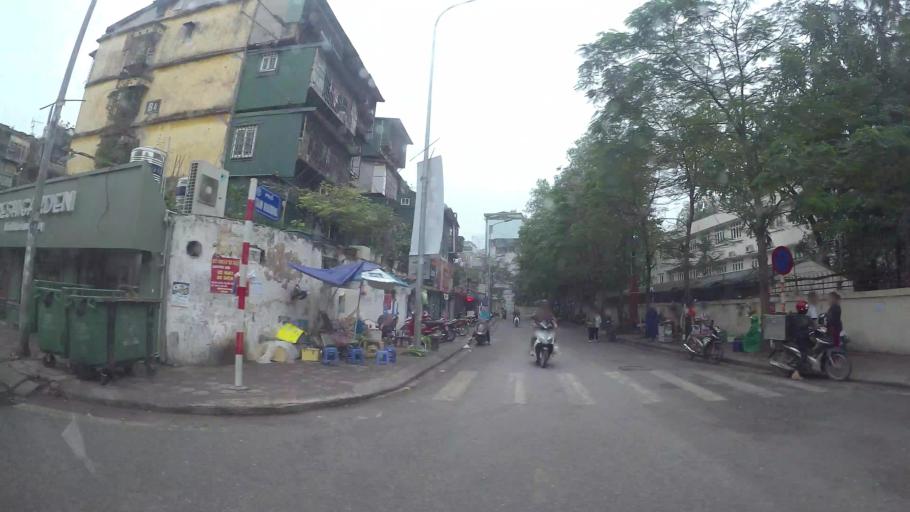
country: VN
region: Ha Noi
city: Dong Da
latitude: 21.0041
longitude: 105.8303
